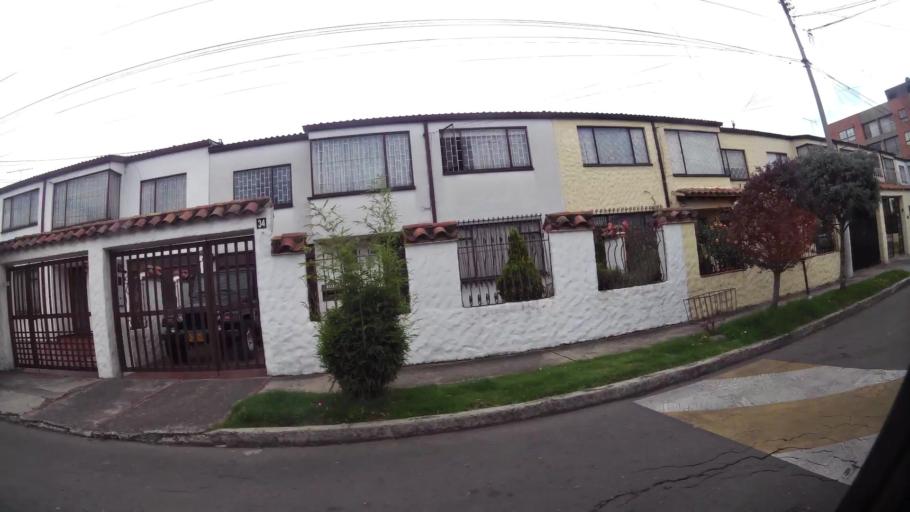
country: CO
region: Bogota D.C.
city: Barrio San Luis
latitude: 4.7161
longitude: -74.0710
